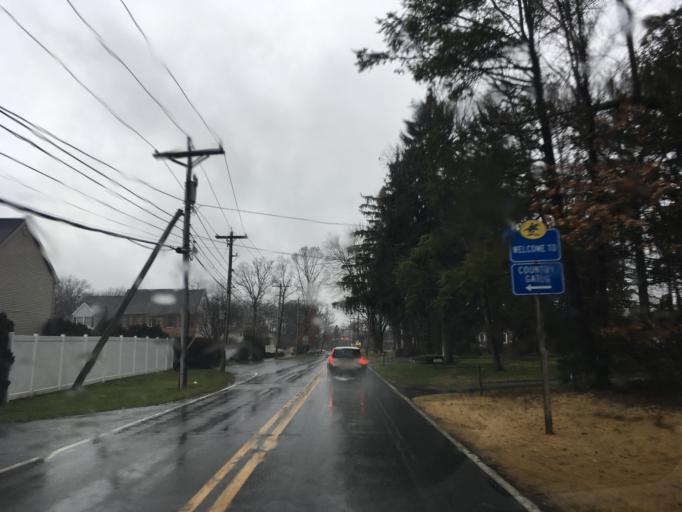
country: US
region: Delaware
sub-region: New Castle County
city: Bellefonte
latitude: 39.8263
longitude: -75.5261
